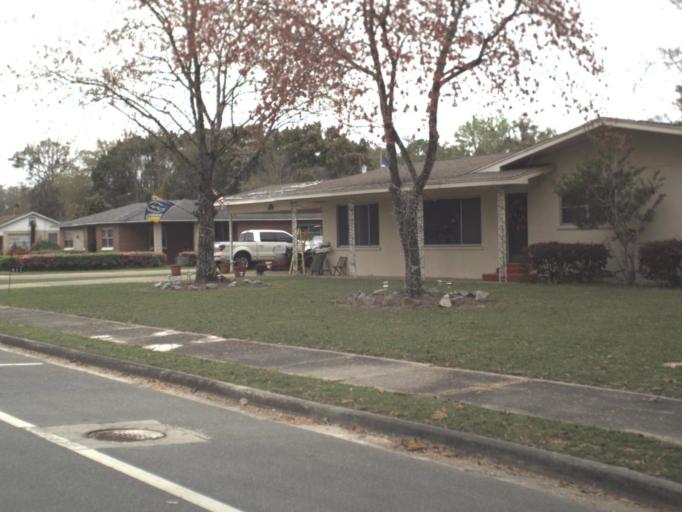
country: US
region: Florida
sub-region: Gulf County
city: Wewahitchka
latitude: 30.1173
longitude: -85.1990
